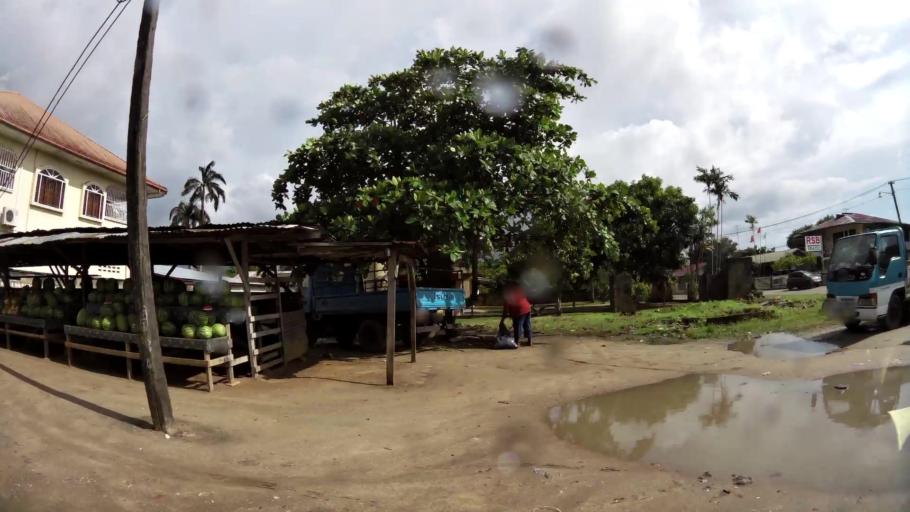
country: SR
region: Paramaribo
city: Paramaribo
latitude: 5.8424
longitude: -55.2060
